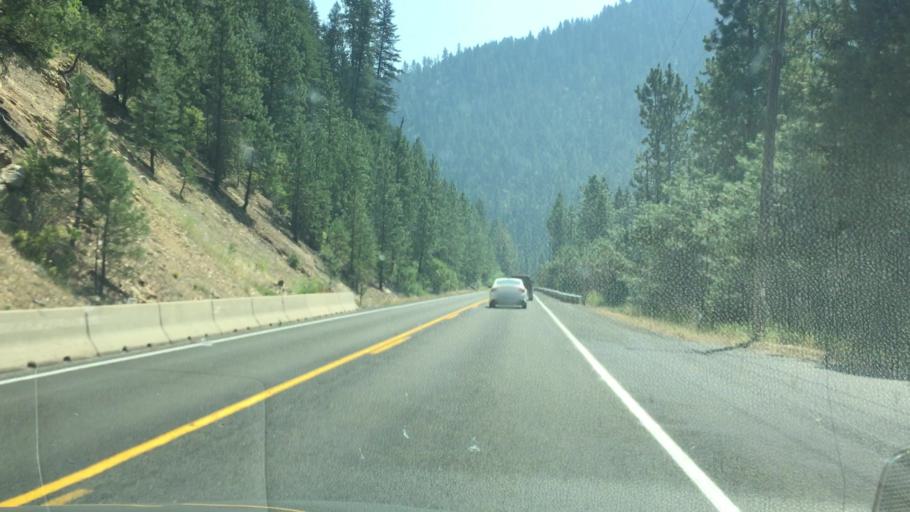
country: US
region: Idaho
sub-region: Valley County
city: McCall
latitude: 45.1540
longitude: -116.2975
